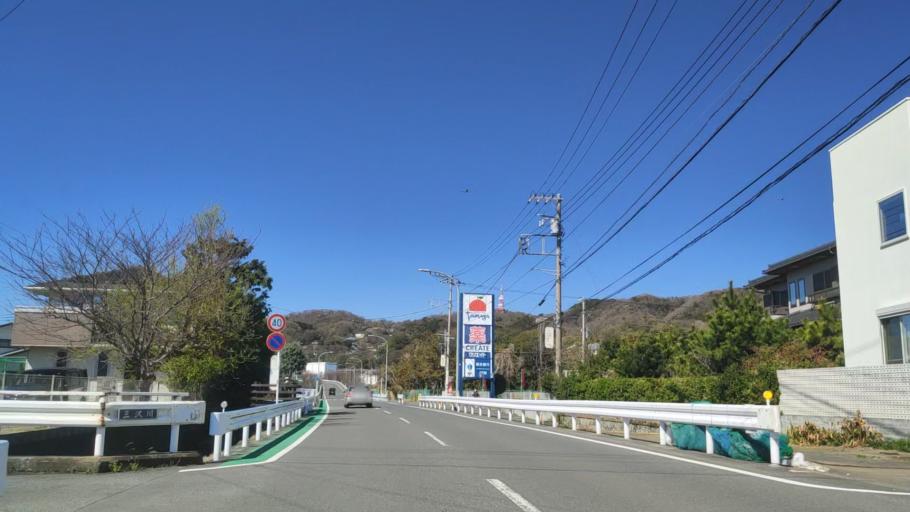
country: JP
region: Kanagawa
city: Hiratsuka
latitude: 35.3169
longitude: 139.3274
